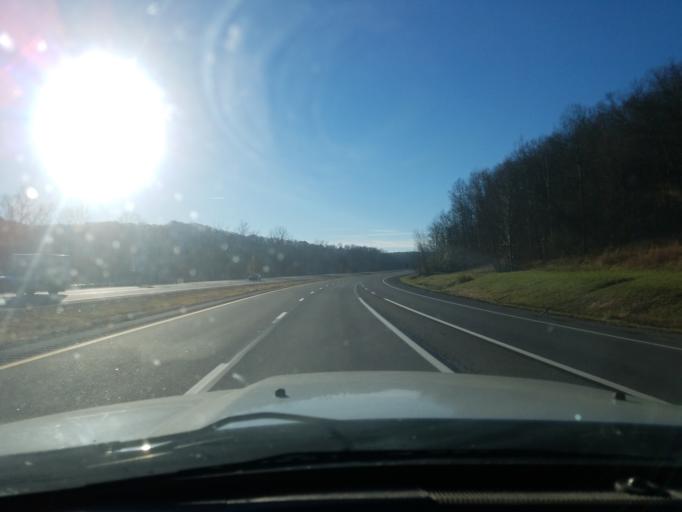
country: US
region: West Virginia
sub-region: Wood County
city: Mineral Wells
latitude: 39.1302
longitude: -81.5476
